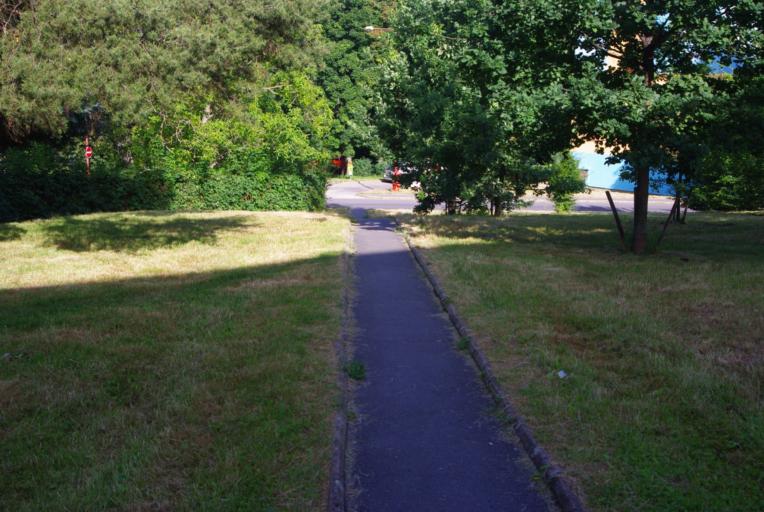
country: SK
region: Banskobystricky
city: Velky Krtis
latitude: 48.2099
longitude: 19.3447
